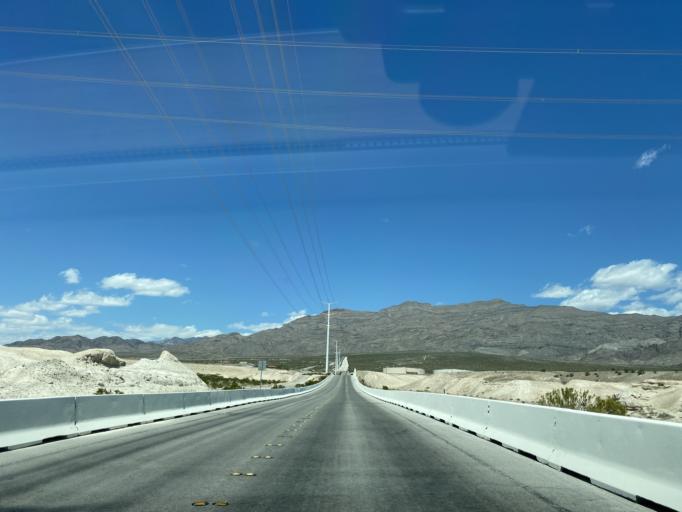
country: US
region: Nevada
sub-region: Clark County
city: North Las Vegas
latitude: 36.3270
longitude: -115.2071
